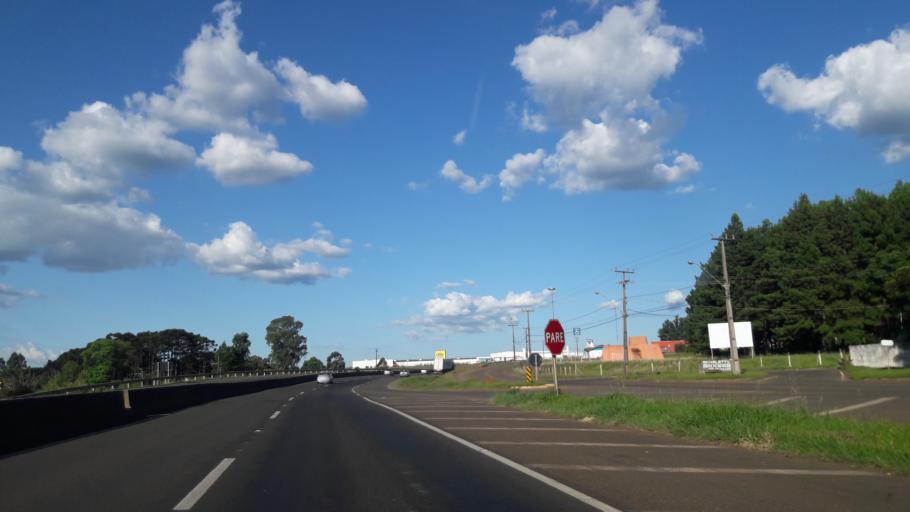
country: BR
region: Parana
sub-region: Guarapuava
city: Guarapuava
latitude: -25.3496
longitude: -51.4561
